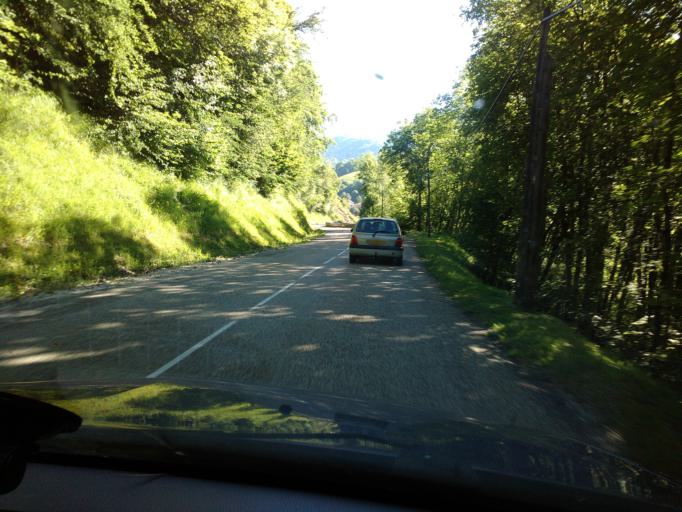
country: FR
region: Rhone-Alpes
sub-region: Departement de l'Isere
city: Saint-Egreve
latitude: 45.2726
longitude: 5.7029
